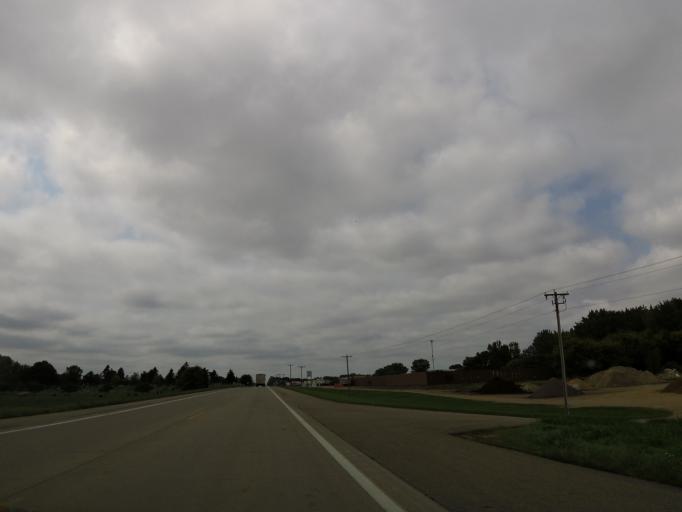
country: US
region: Minnesota
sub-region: Lac qui Parle County
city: Dawson
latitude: 44.9359
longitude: -96.0374
